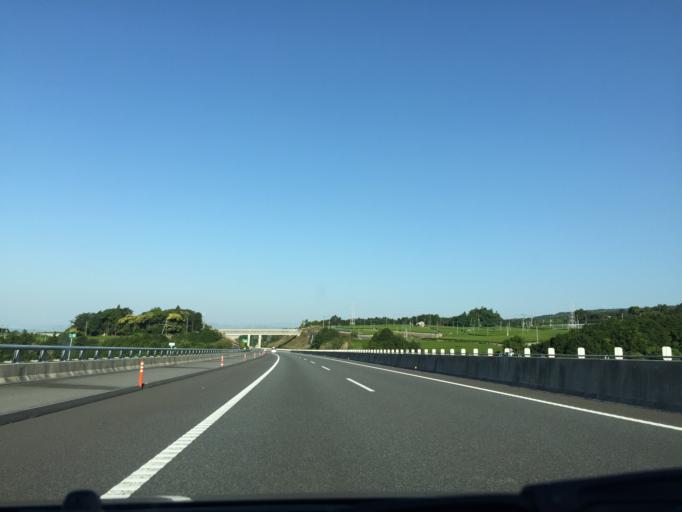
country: JP
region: Shizuoka
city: Numazu
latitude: 35.1548
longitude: 138.8273
